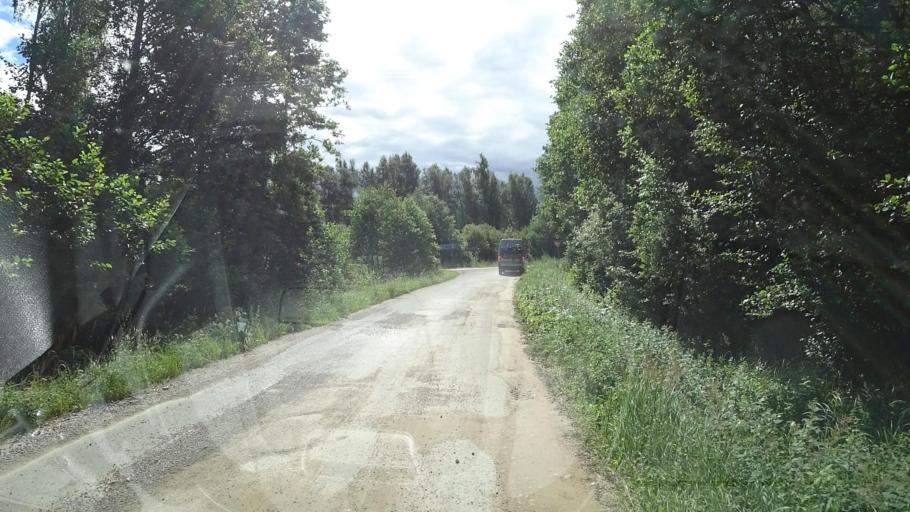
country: LV
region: Ventspils
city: Ventspils
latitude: 57.4873
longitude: 21.6752
